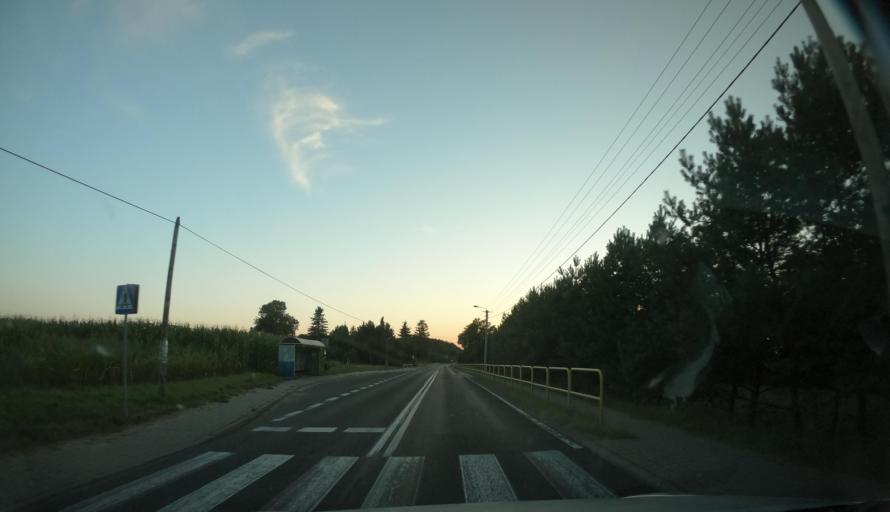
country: PL
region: Kujawsko-Pomorskie
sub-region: Powiat bydgoski
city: Koronowo
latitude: 53.3281
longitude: 17.9030
